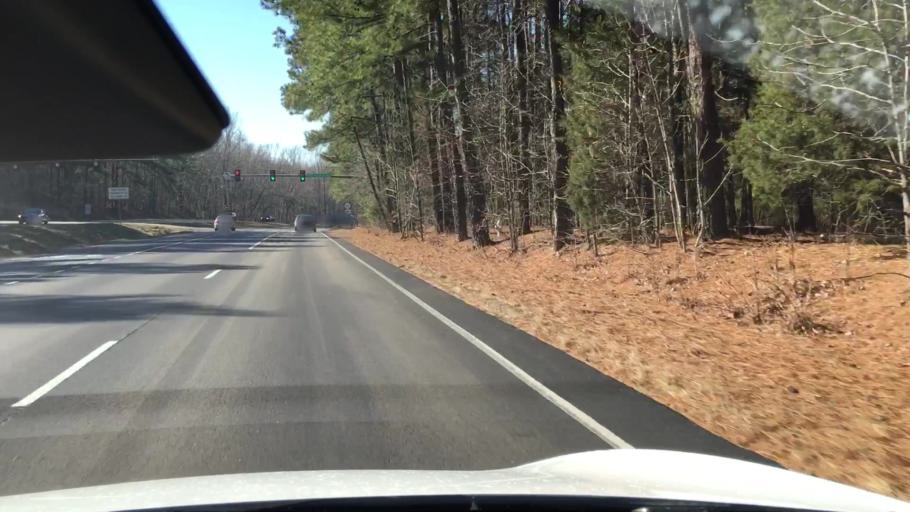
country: US
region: Virginia
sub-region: Chesterfield County
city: Woodlake
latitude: 37.5054
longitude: -77.7162
